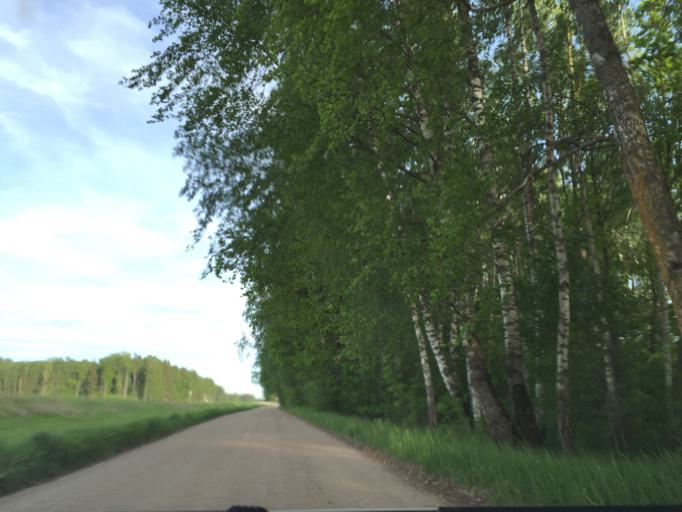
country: LV
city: Tireli
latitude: 56.6801
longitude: 23.5004
